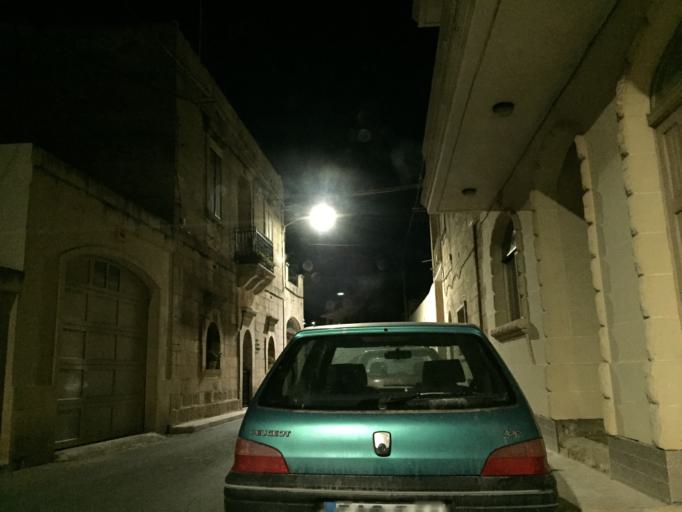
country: MT
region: Ix-Xaghra
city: Xaghra
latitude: 36.0477
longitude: 14.2629
